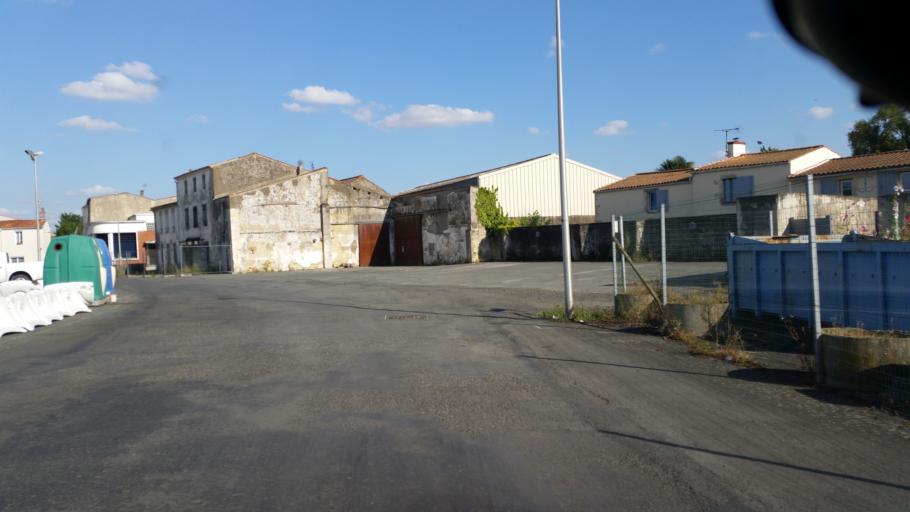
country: FR
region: Poitou-Charentes
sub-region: Departement de la Charente-Maritime
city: Marans
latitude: 46.3123
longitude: -0.9991
